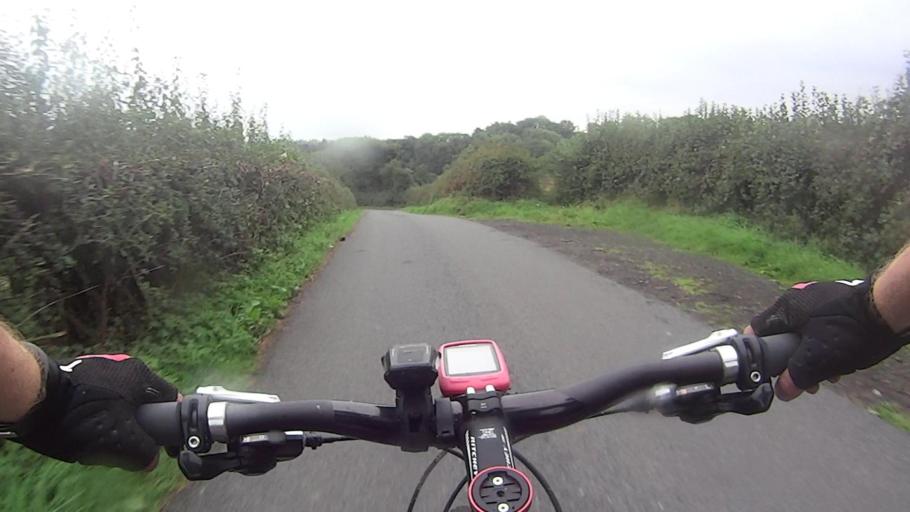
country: GB
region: England
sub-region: Worcestershire
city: Tenbury Wells
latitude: 52.2967
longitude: -2.5597
